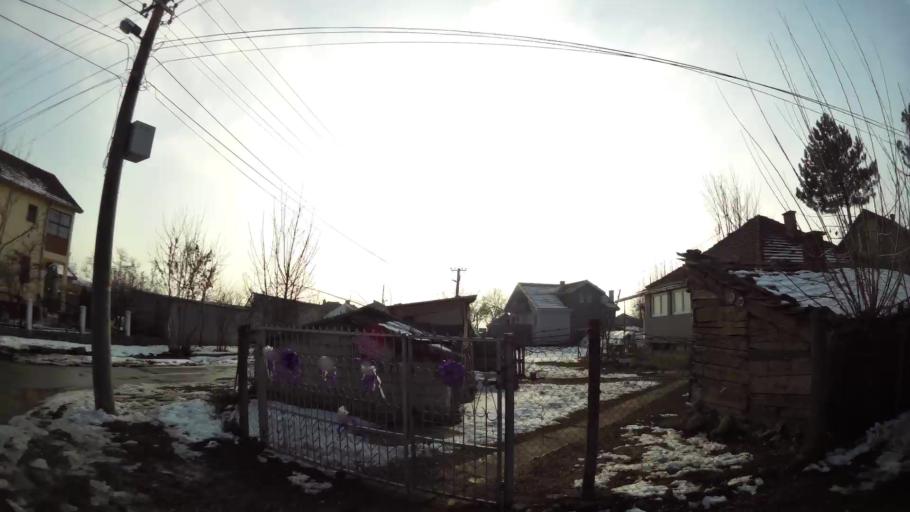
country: MK
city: Miladinovci
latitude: 41.9751
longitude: 21.6466
